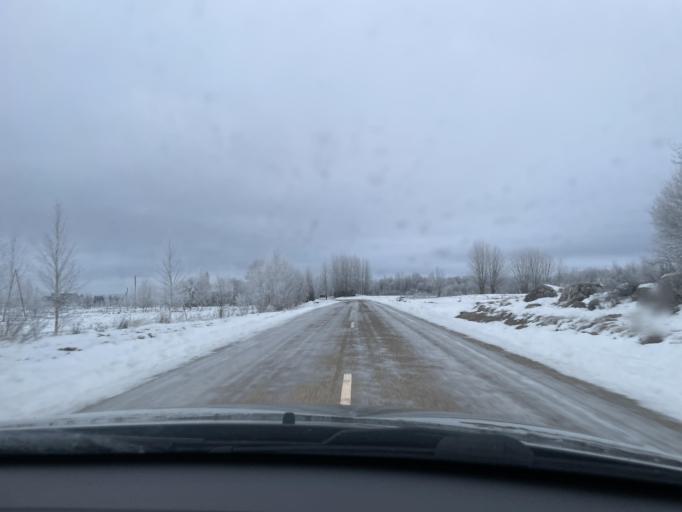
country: LV
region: Ludzas Rajons
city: Ludza
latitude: 56.4580
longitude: 27.5667
